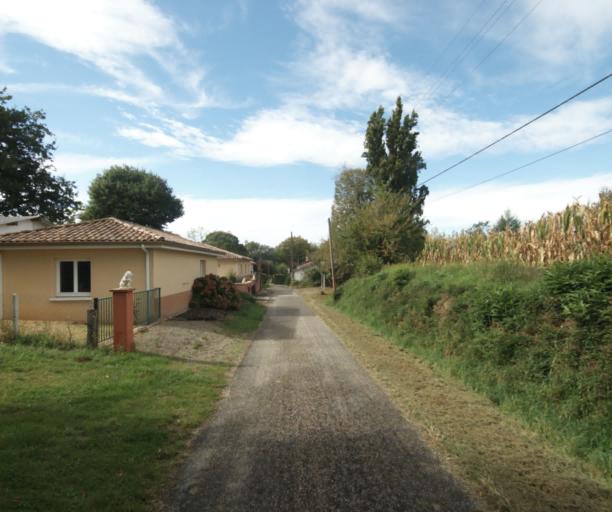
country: FR
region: Aquitaine
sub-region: Departement des Landes
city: Villeneuve-de-Marsan
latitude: 43.8956
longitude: -0.2026
